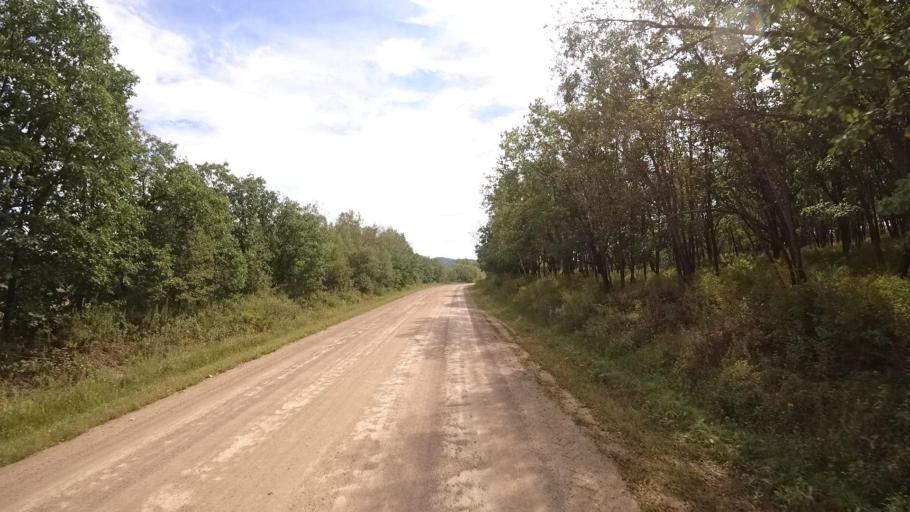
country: RU
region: Primorskiy
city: Yakovlevka
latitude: 44.5989
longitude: 133.6054
